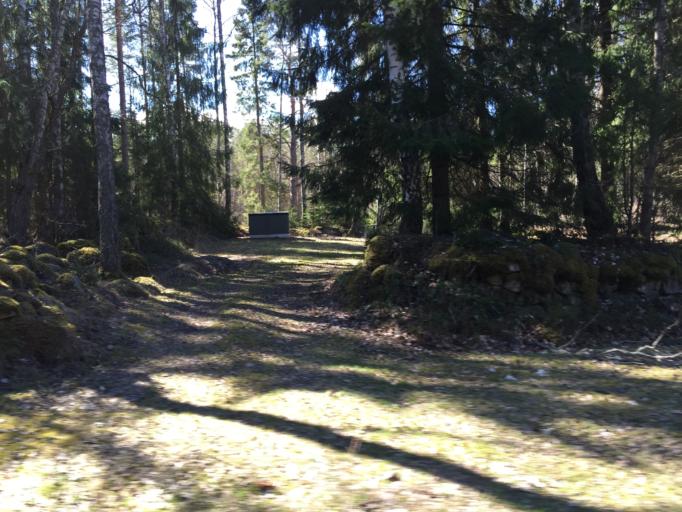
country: SE
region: OEstergoetland
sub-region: Finspangs Kommun
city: Finspang
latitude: 58.8879
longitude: 15.7387
